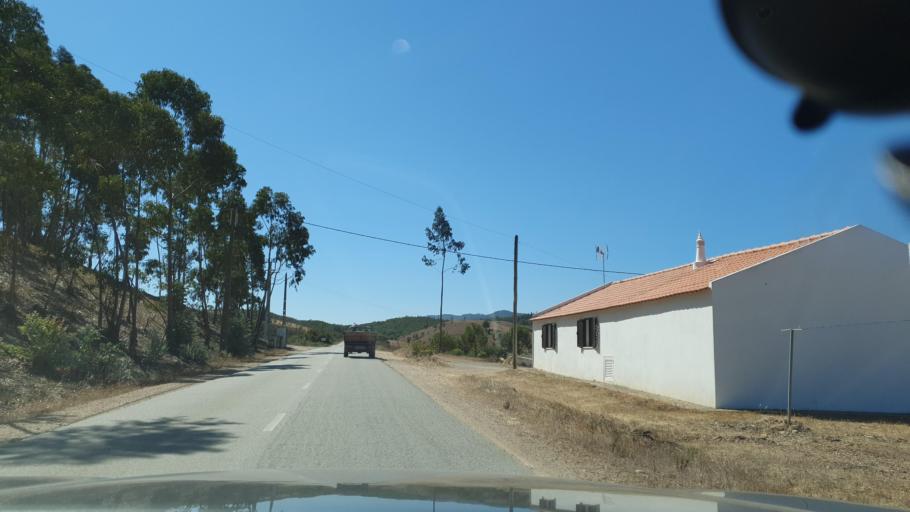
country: PT
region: Beja
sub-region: Odemira
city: Sao Teotonio
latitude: 37.4762
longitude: -8.6256
